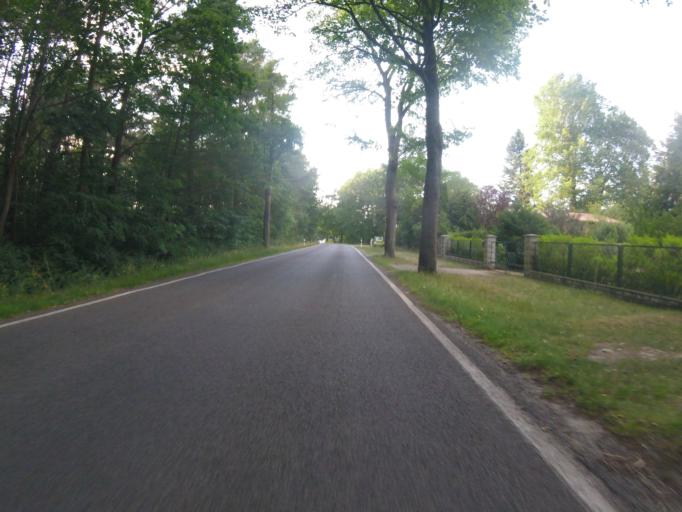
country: DE
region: Brandenburg
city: Mittenwalde
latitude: 52.2018
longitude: 13.5728
